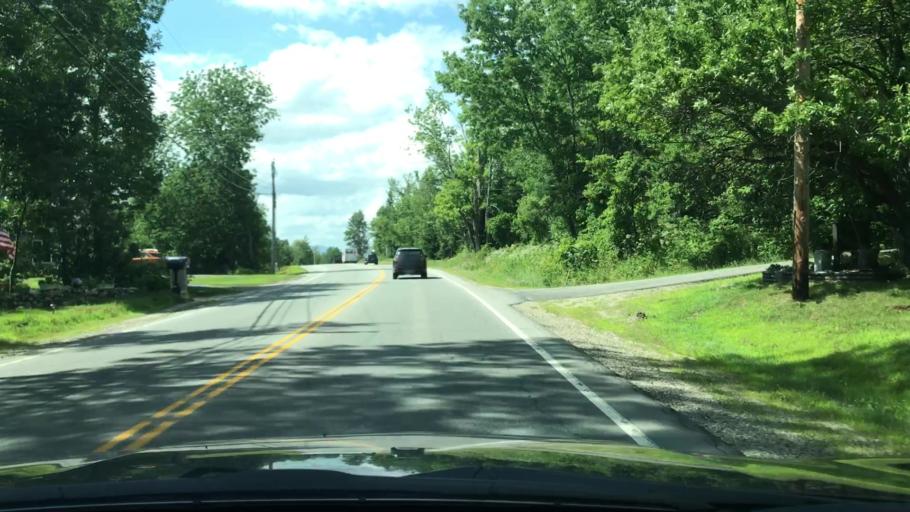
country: US
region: New Hampshire
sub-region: Coos County
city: Jefferson
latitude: 44.3729
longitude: -71.4082
